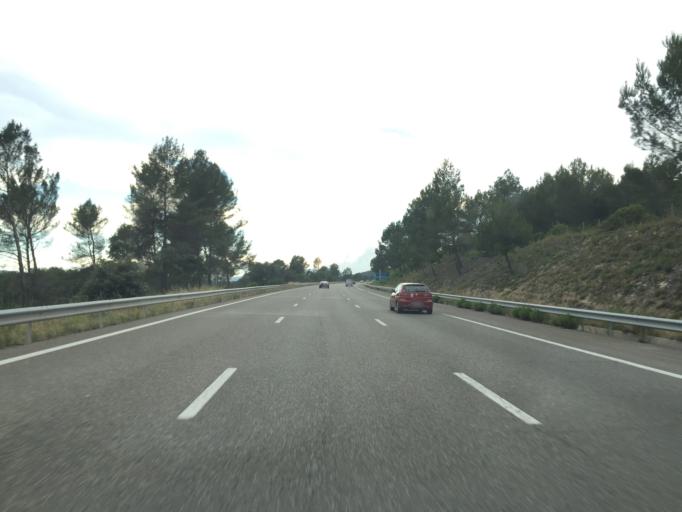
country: FR
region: Provence-Alpes-Cote d'Azur
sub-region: Departement du Var
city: La Celle
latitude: 43.4188
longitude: 6.0240
